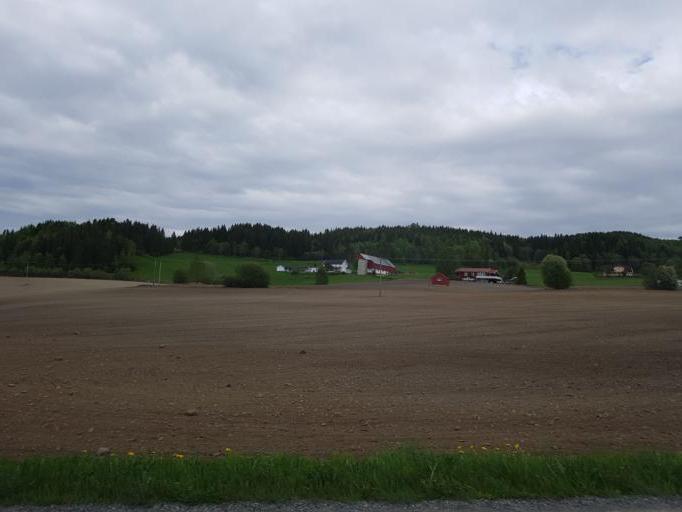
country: NO
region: Nord-Trondelag
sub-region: Levanger
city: Levanger
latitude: 63.7130
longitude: 11.2511
